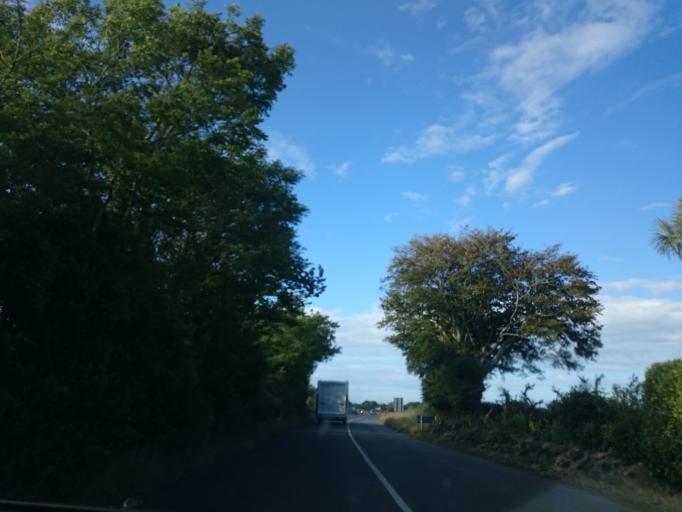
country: IE
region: Leinster
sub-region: Loch Garman
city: Loch Garman
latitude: 52.2251
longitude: -6.5065
